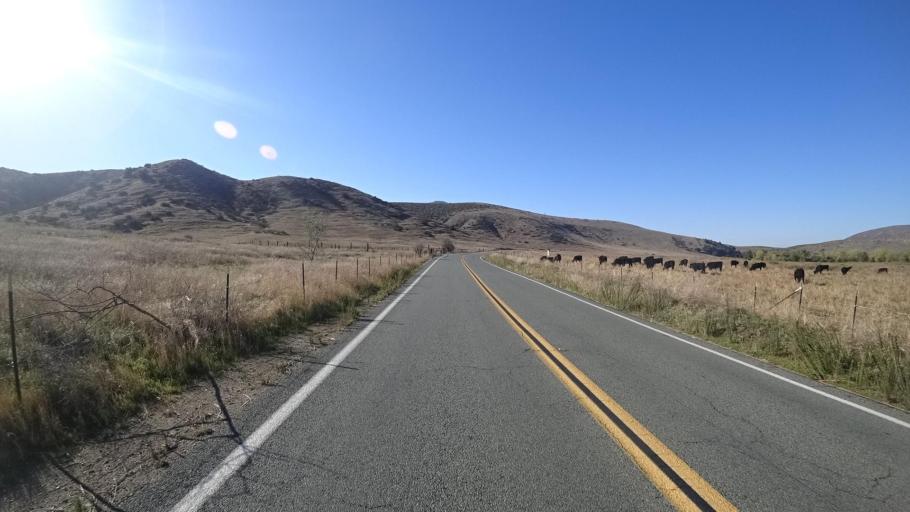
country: US
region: California
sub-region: San Diego County
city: Jamul
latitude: 32.6629
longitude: -116.8376
